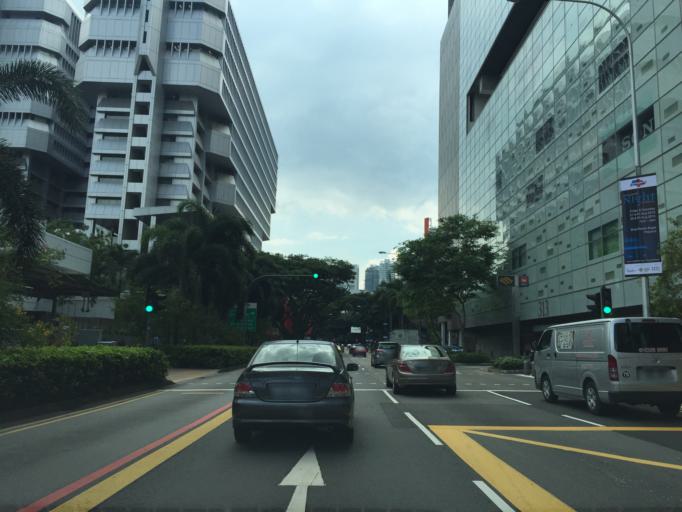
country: SG
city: Singapore
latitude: 1.3004
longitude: 103.8387
